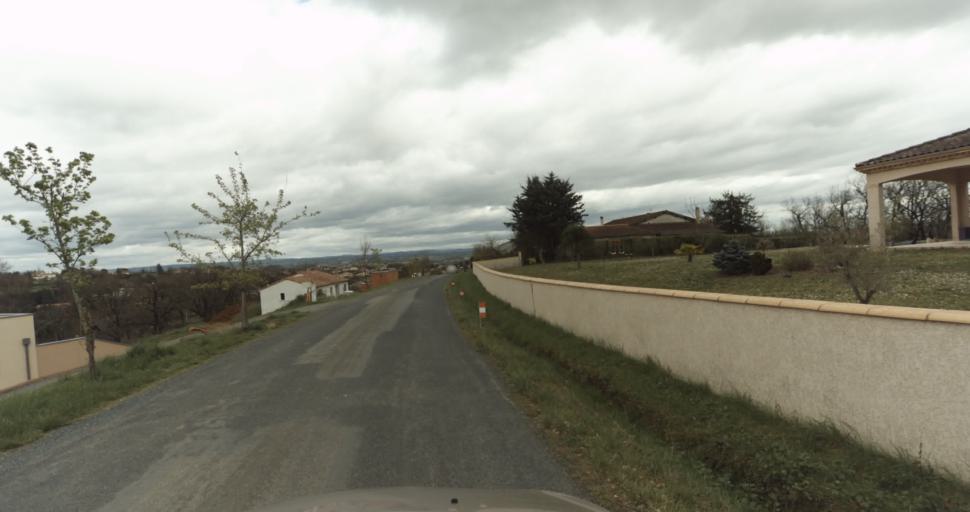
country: FR
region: Midi-Pyrenees
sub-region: Departement du Tarn
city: Puygouzon
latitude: 43.9010
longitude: 2.1663
